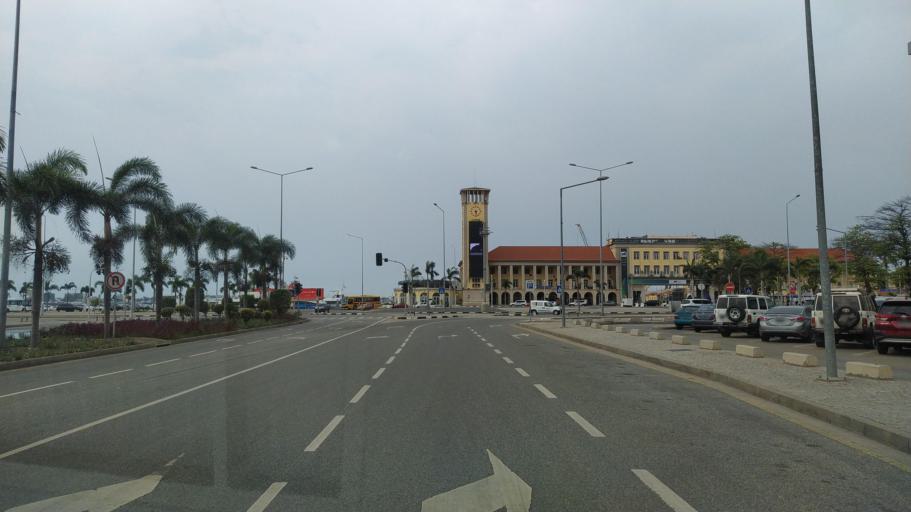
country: AO
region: Luanda
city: Luanda
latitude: -8.8036
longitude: 13.2413
